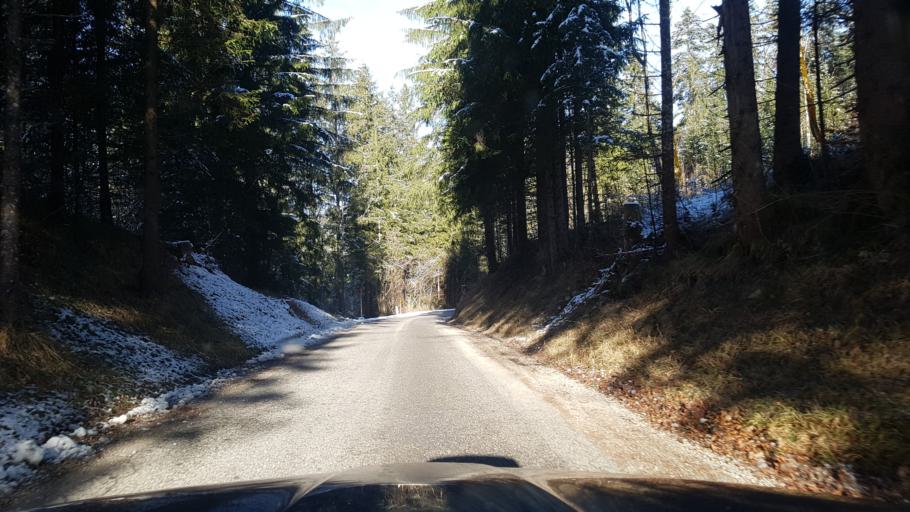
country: AT
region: Salzburg
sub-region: Politischer Bezirk Salzburg-Umgebung
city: Faistenau
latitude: 47.7706
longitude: 13.2224
